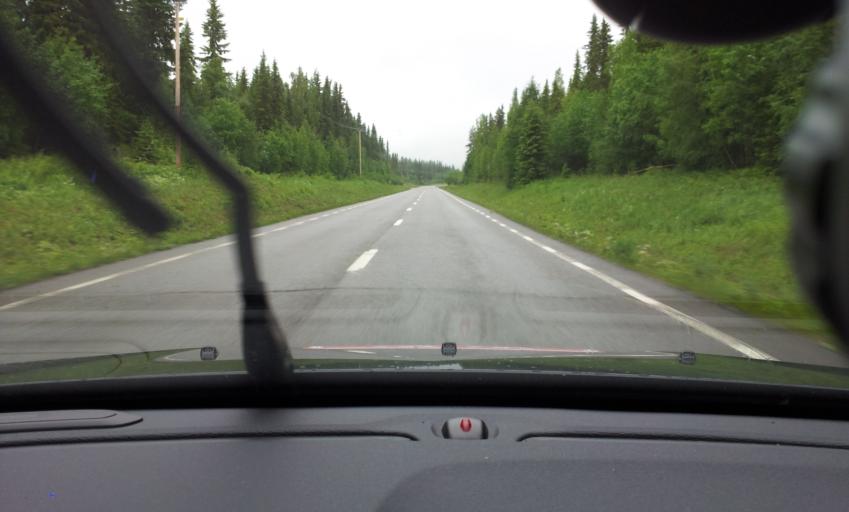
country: SE
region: Jaemtland
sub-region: Krokoms Kommun
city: Krokom
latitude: 63.4882
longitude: 14.5058
